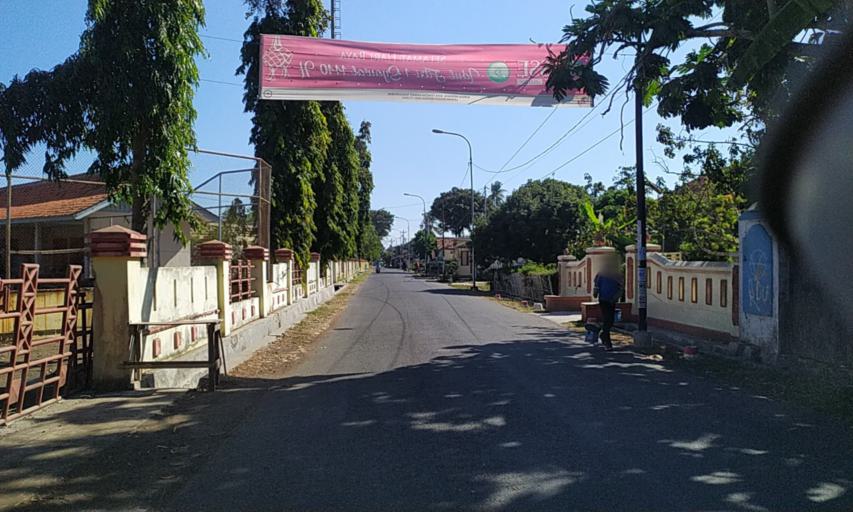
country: ID
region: Central Java
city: Rejanegara
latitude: -7.6941
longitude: 109.0346
